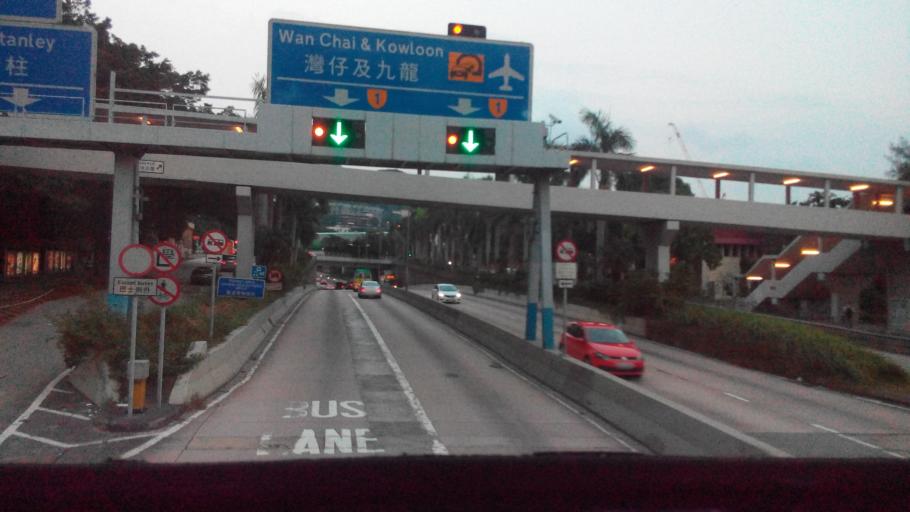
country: HK
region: Wanchai
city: Wan Chai
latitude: 22.2504
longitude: 114.1724
